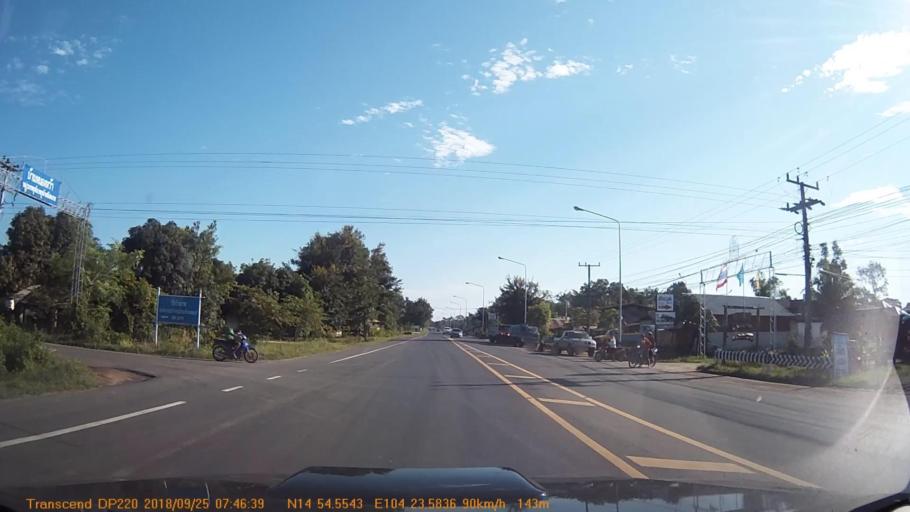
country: TH
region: Sisaket
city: Phayu
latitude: 14.9094
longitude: 104.3932
